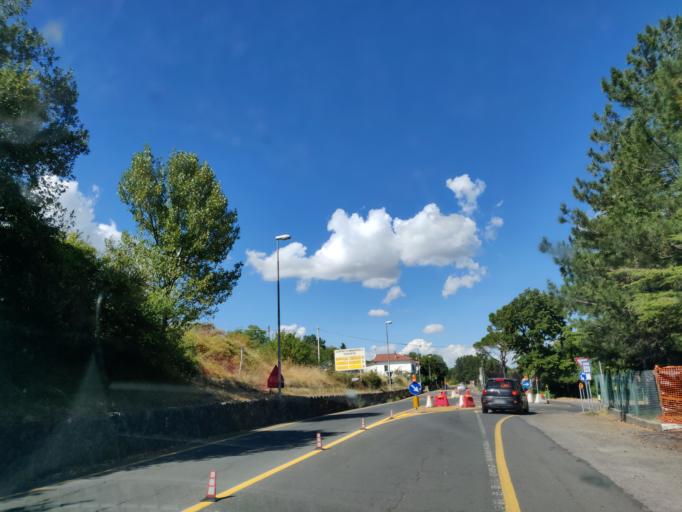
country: IT
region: Tuscany
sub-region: Provincia di Siena
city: Abbadia San Salvatore
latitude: 42.8928
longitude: 11.6676
